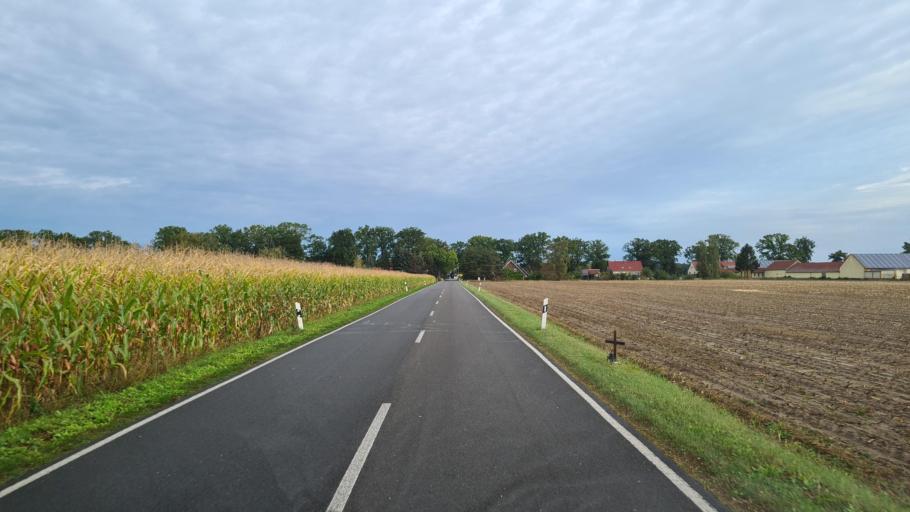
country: DE
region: Brandenburg
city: Kasel-Golzig
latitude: 51.9309
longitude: 13.7070
